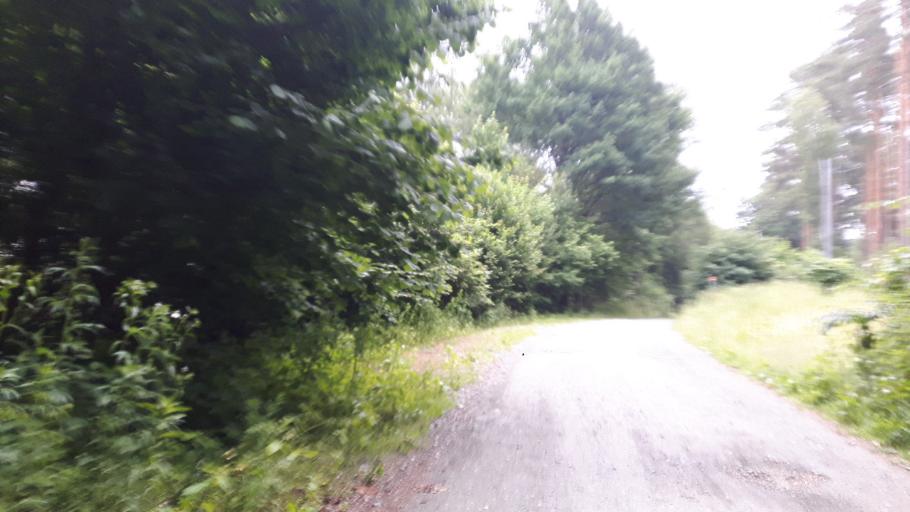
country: PL
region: Warmian-Masurian Voivodeship
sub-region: Powiat elblaski
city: Tolkmicko
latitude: 54.3366
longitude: 19.5580
